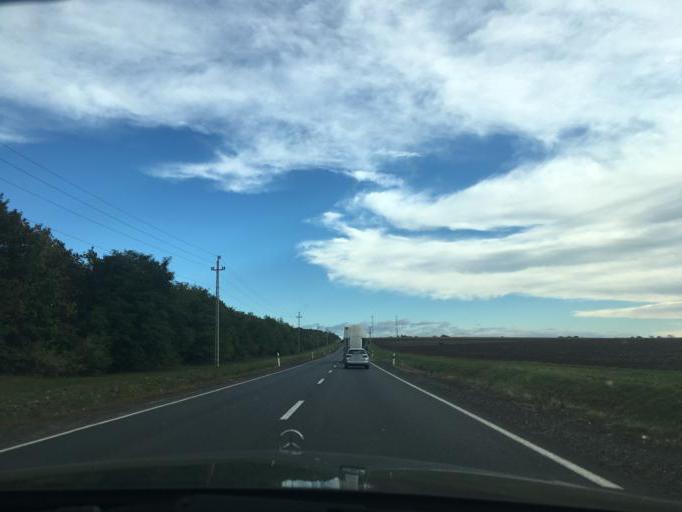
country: HU
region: Borsod-Abauj-Zemplen
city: Arnot
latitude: 48.1439
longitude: 20.8885
